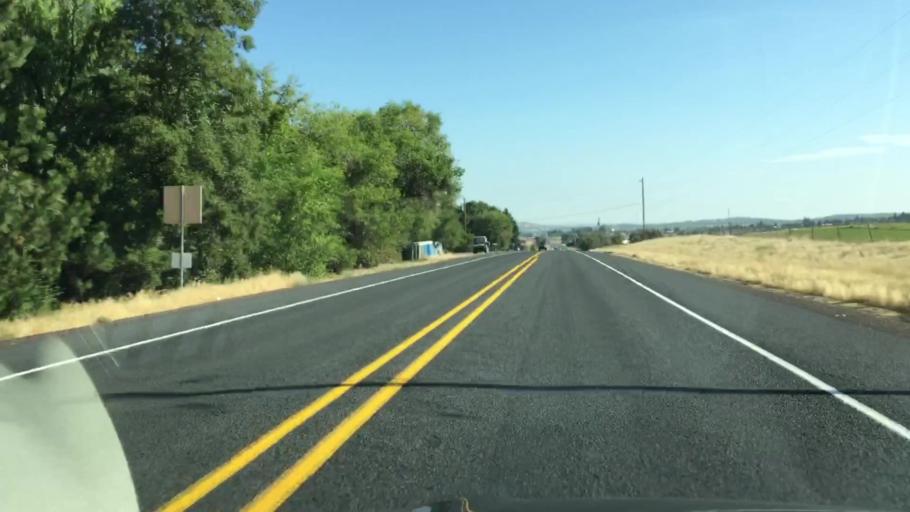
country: US
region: Oregon
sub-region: Jefferson County
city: Madras
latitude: 44.5930
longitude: -121.1477
